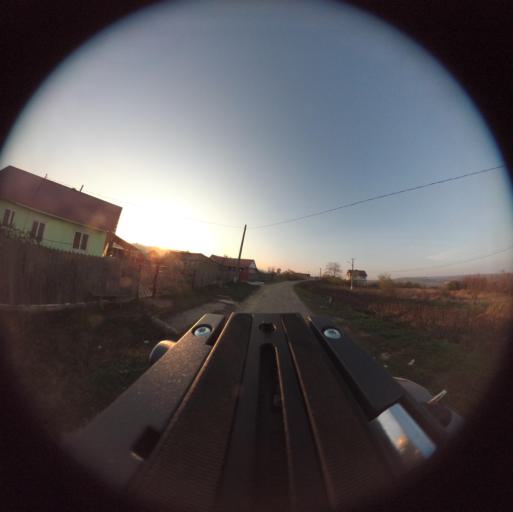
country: RO
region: Vaslui
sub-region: Comuna Bacesti
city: Bacesti
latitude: 46.8285
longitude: 27.2493
